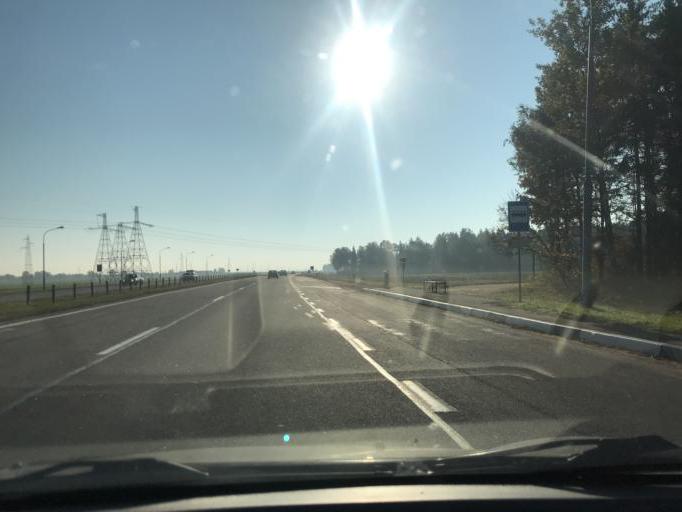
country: BY
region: Minsk
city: Dukora
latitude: 53.6196
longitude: 28.0498
